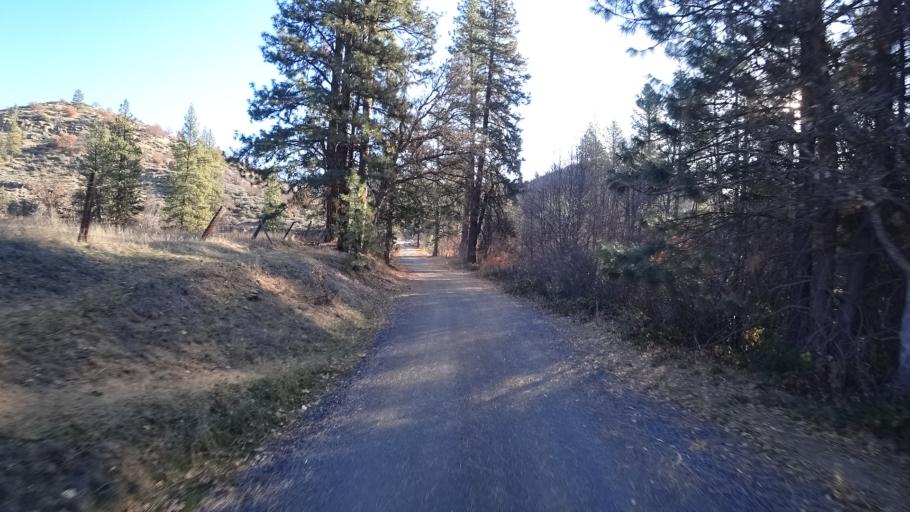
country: US
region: Oregon
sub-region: Jackson County
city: Ashland
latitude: 41.9777
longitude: -122.6314
